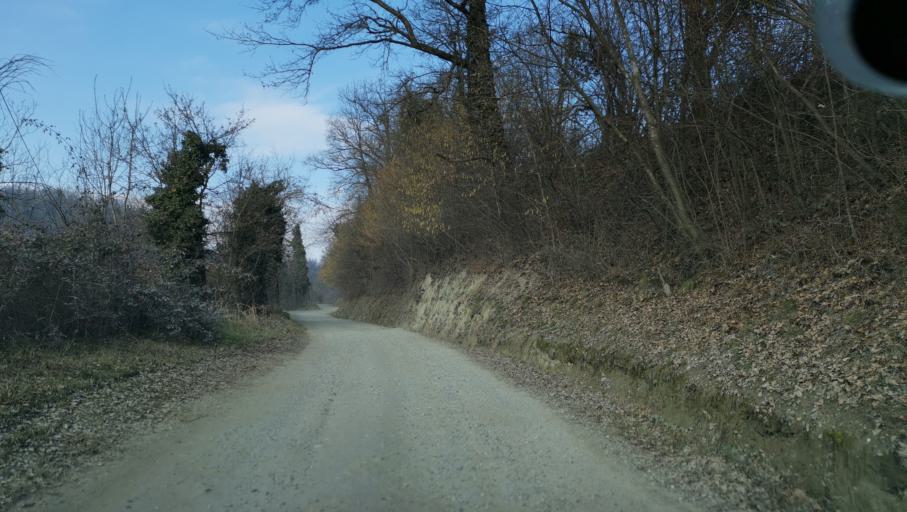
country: IT
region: Piedmont
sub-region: Provincia di Torino
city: Gassino Torinese
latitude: 45.1047
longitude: 7.8423
